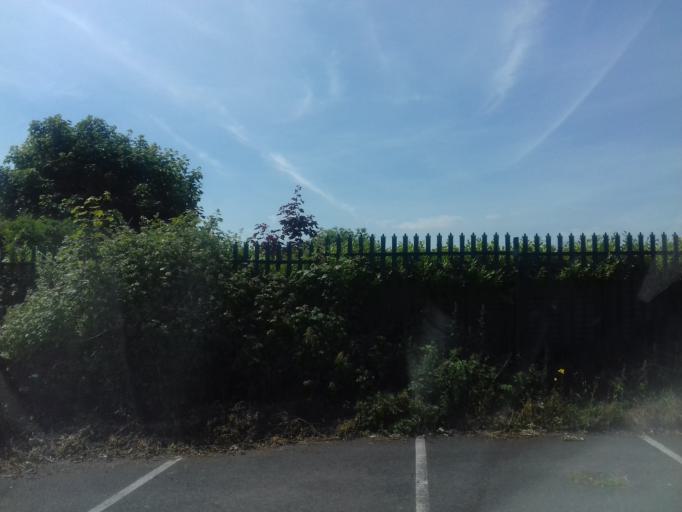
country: IE
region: Leinster
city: Lusk
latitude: 53.5188
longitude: -6.1451
